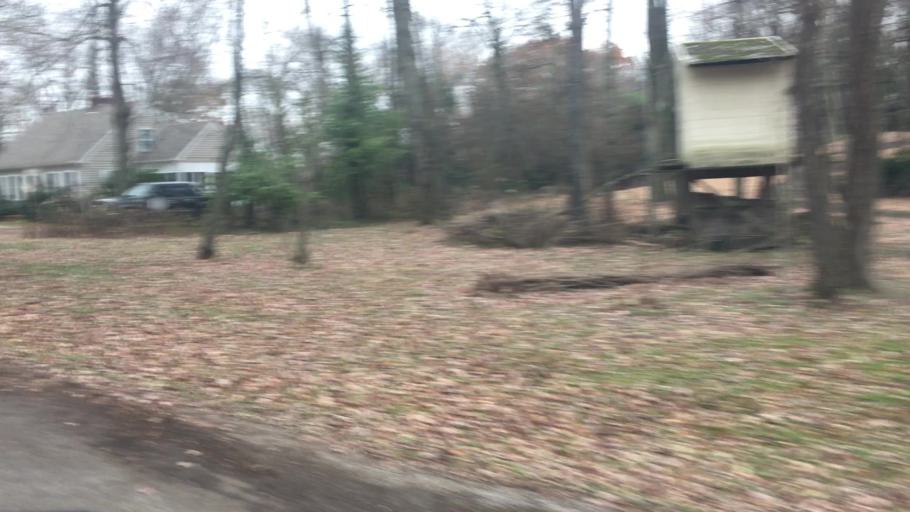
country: US
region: Pennsylvania
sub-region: Lawrence County
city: Bessemer
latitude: 40.9626
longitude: -80.4328
